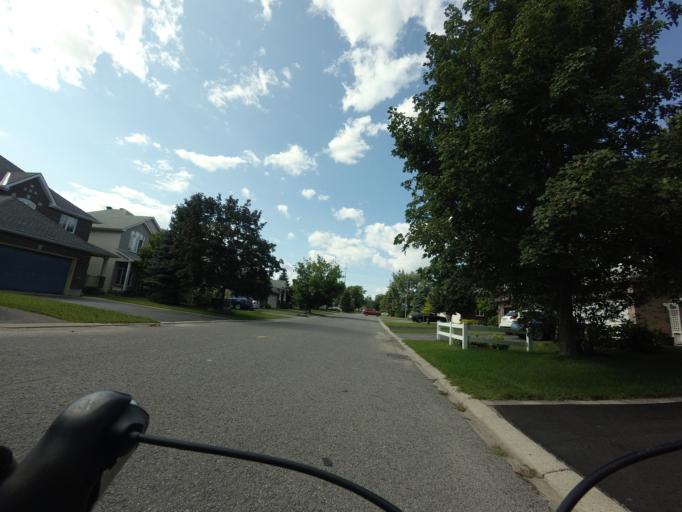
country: CA
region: Ontario
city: Bells Corners
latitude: 45.2868
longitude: -75.8481
